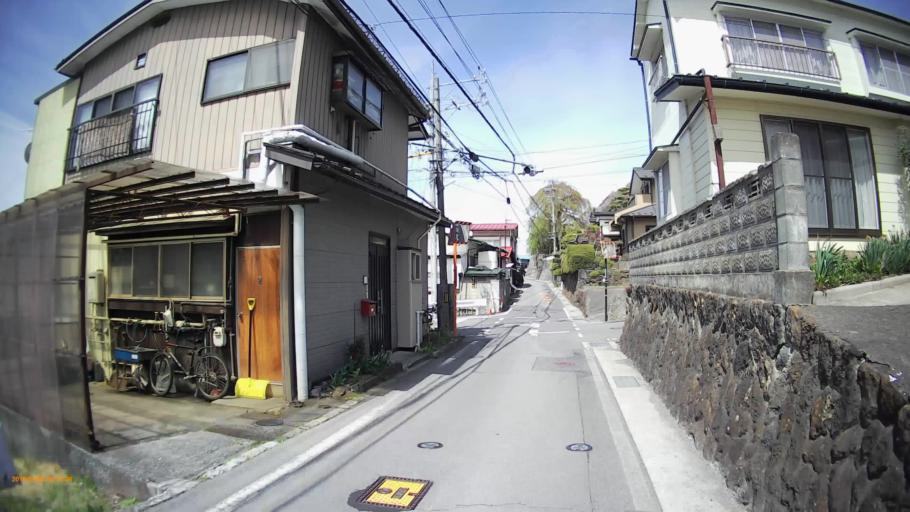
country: JP
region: Nagano
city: Suwa
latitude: 36.0667
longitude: 138.1045
